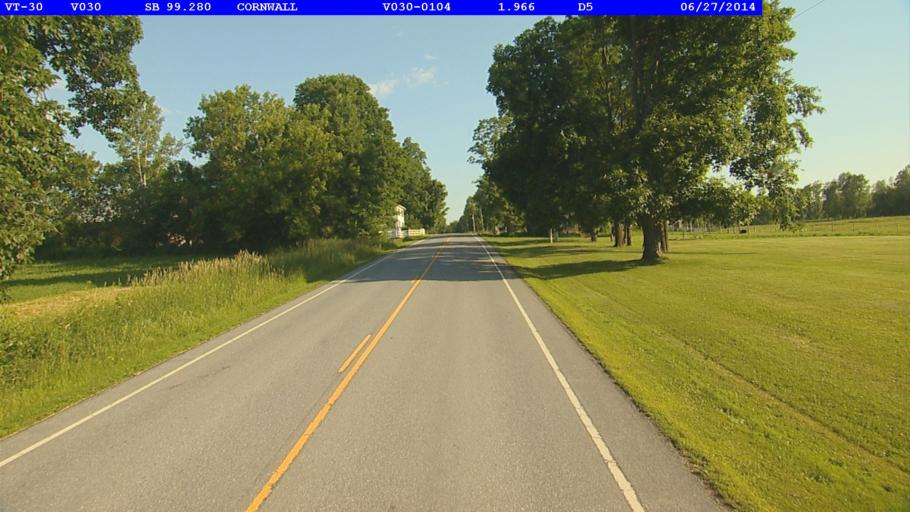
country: US
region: Vermont
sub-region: Addison County
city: Middlebury (village)
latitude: 43.9360
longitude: -73.2125
